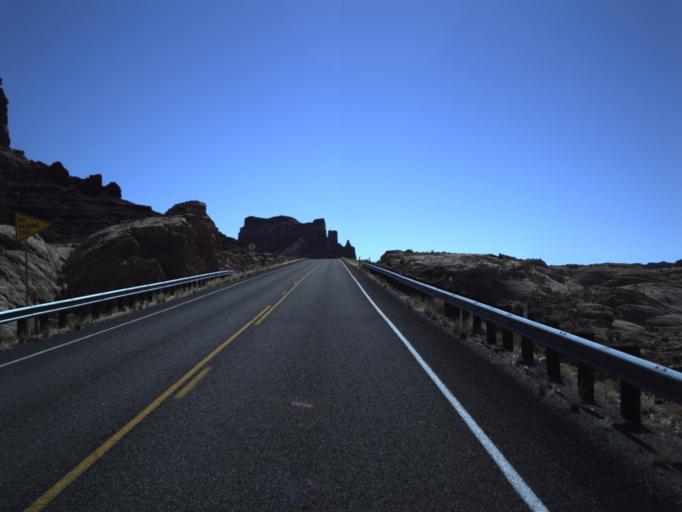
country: US
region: Utah
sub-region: San Juan County
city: Blanding
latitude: 37.9112
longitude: -110.3864
